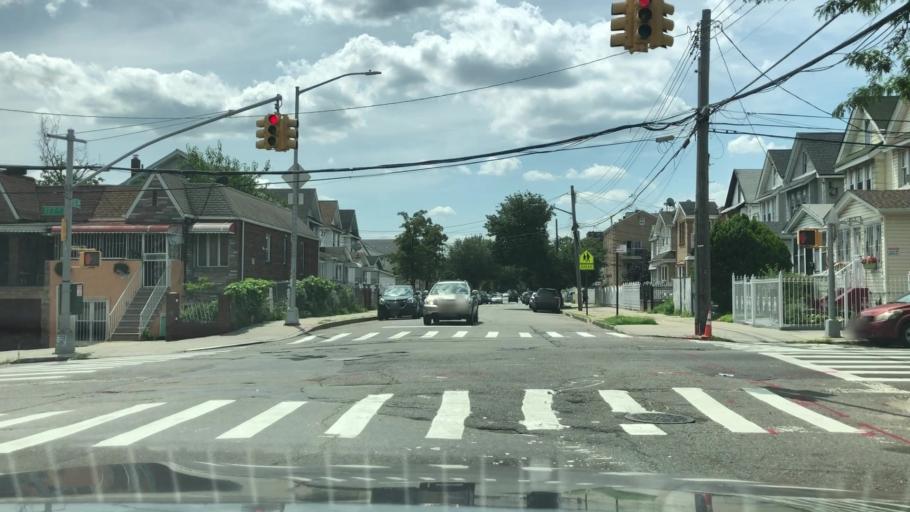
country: US
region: New York
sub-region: Queens County
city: Jamaica
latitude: 40.7069
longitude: -73.7832
